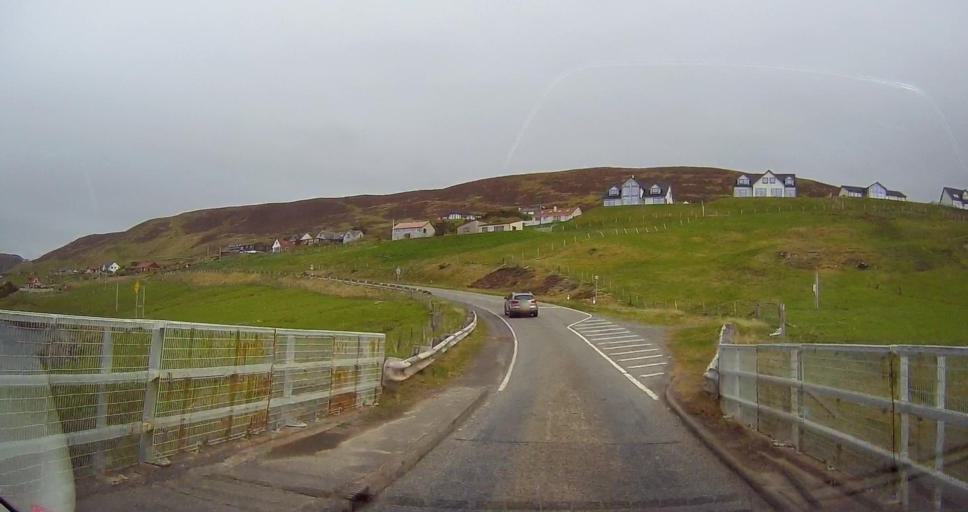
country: GB
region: Scotland
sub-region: Shetland Islands
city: Lerwick
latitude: 60.1293
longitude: -1.2723
